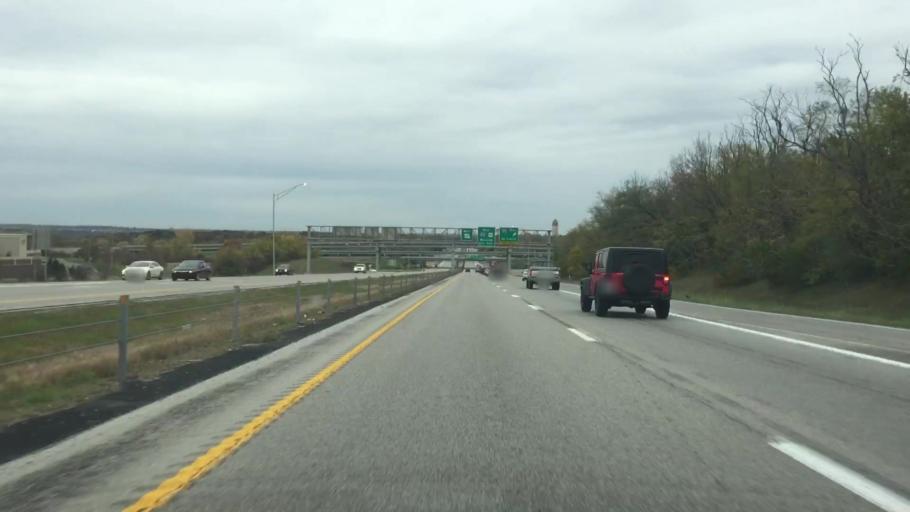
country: US
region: Missouri
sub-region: Jackson County
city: Lees Summit
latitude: 38.9286
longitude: -94.4048
